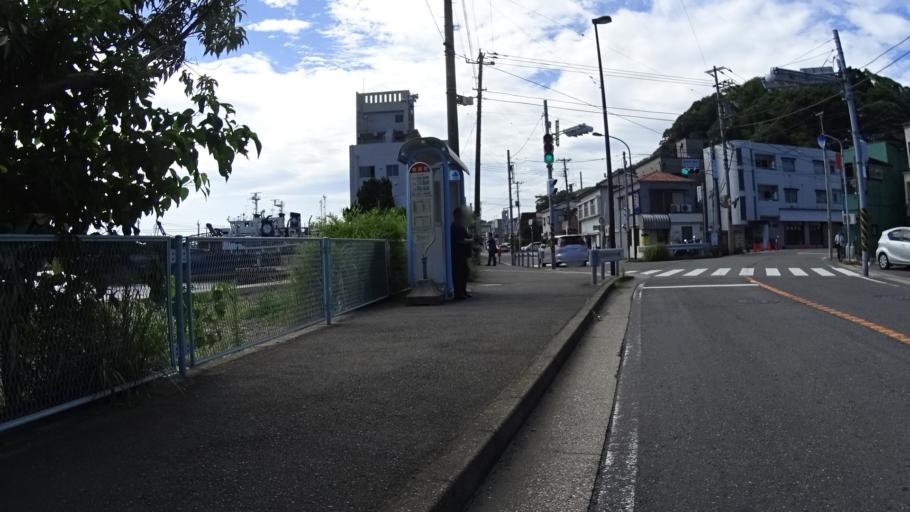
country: JP
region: Kanagawa
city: Yokosuka
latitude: 35.2417
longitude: 139.7190
